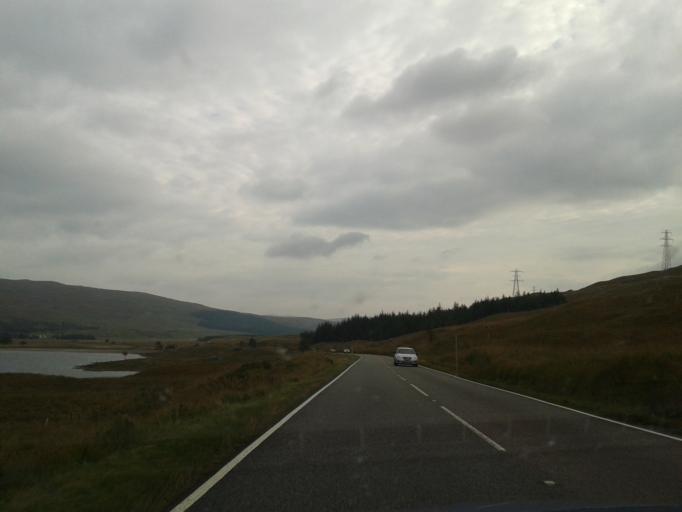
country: GB
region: Scotland
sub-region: Highland
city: Spean Bridge
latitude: 56.5499
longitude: -4.7543
